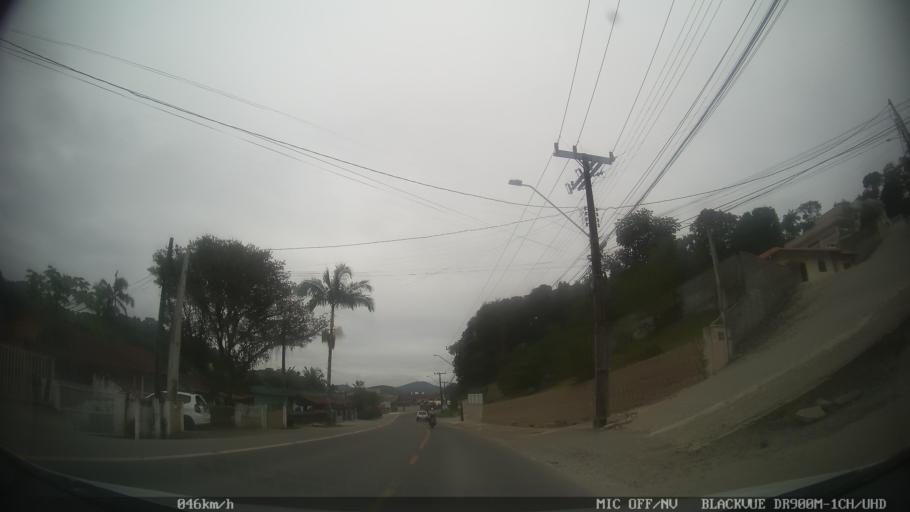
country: BR
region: Santa Catarina
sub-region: Joinville
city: Joinville
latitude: -26.3482
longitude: -48.8183
